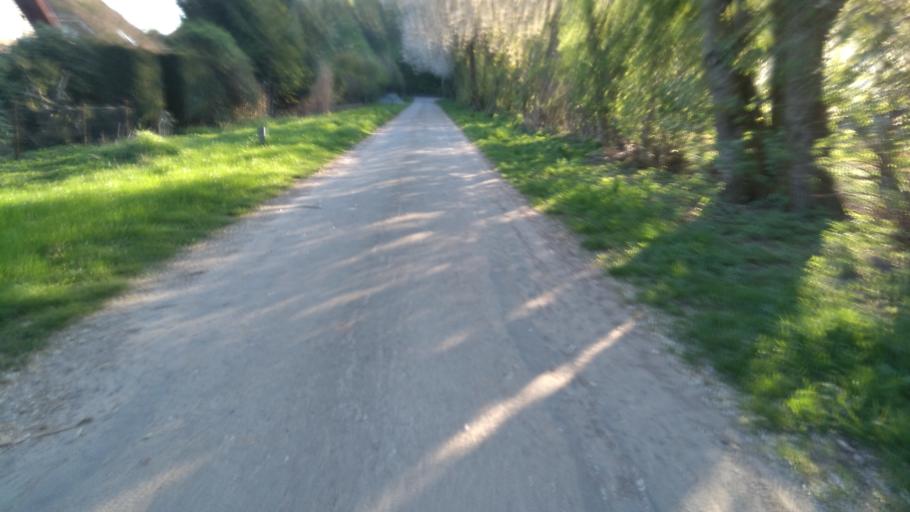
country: DE
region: Lower Saxony
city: Nottensdorf
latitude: 53.4743
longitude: 9.6148
